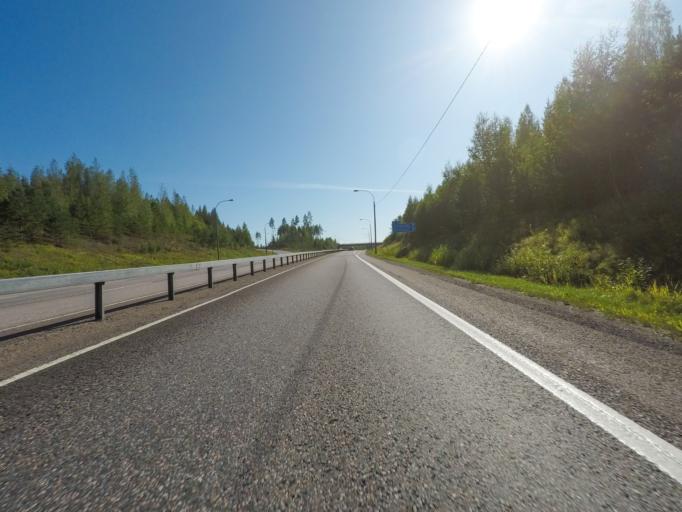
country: FI
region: Southern Savonia
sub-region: Pieksaemaeki
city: Joroinen
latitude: 62.2278
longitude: 27.8891
